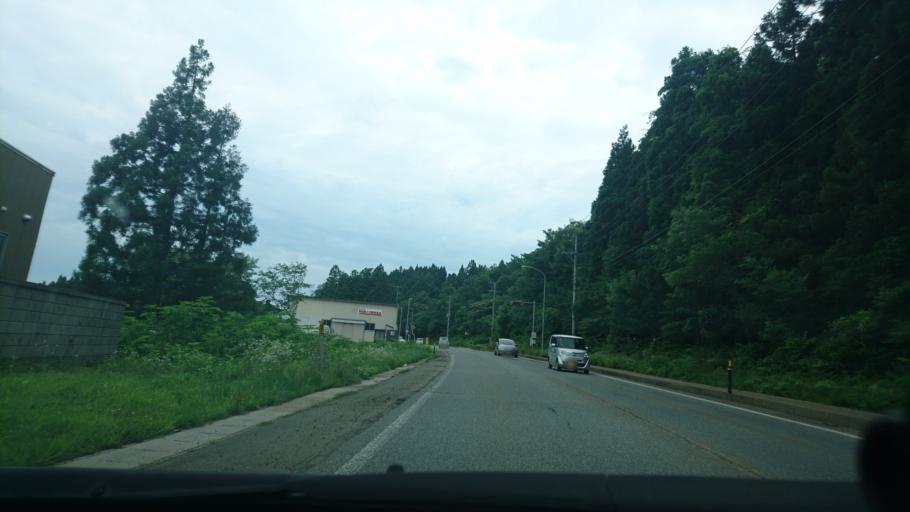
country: JP
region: Akita
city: Yokotemachi
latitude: 39.3362
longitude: 140.5606
